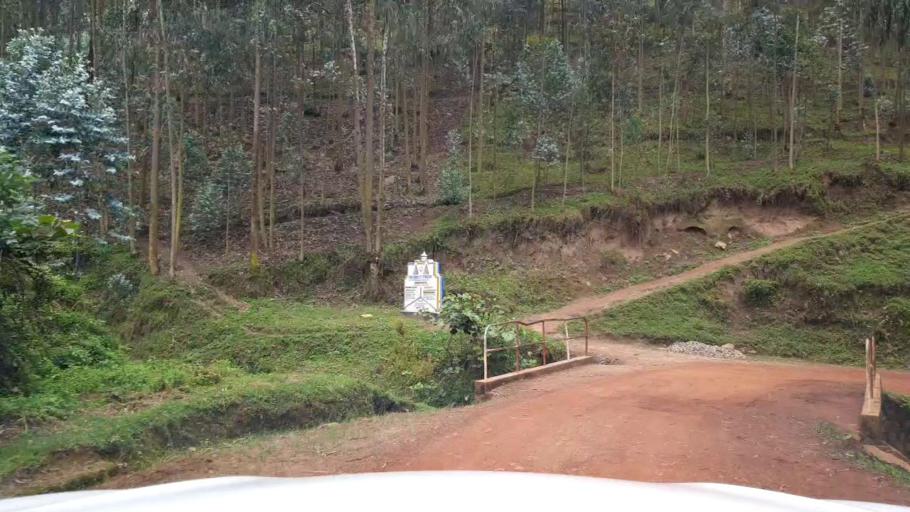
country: UG
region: Western Region
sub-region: Kabale District
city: Kabale
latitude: -1.4327
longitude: 29.8706
